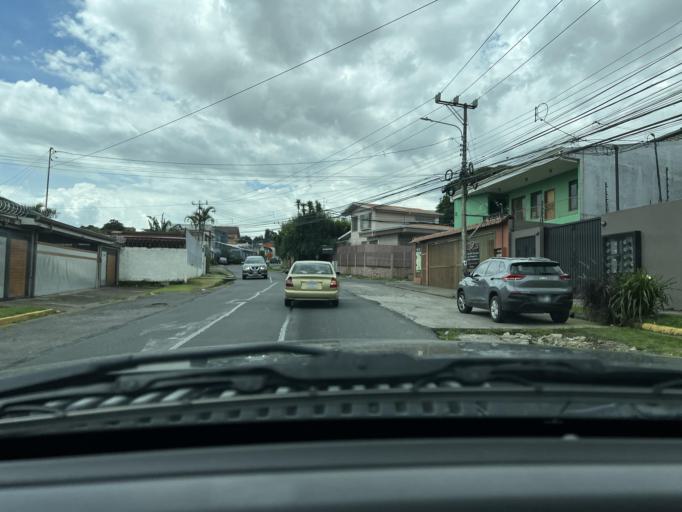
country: CR
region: San Jose
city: Granadilla
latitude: 9.9382
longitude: -84.0261
